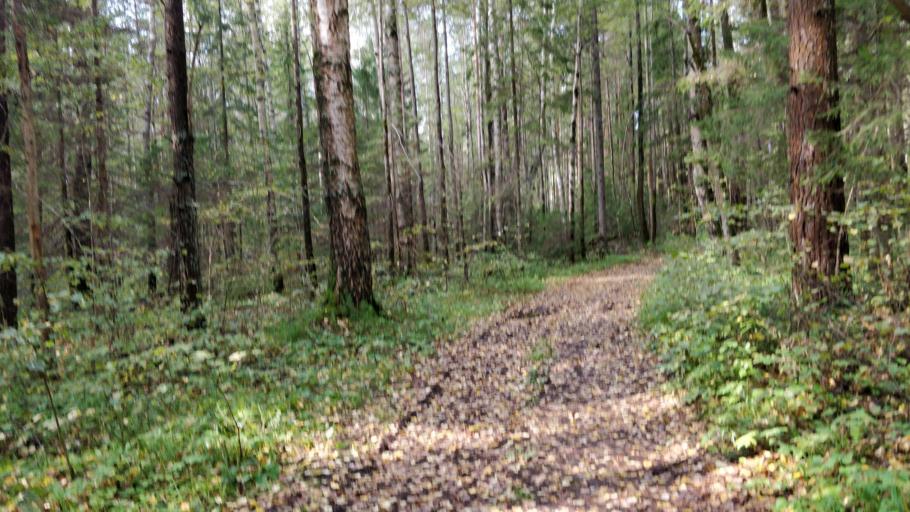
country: RU
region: Perm
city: Perm
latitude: 58.0758
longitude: 56.2113
